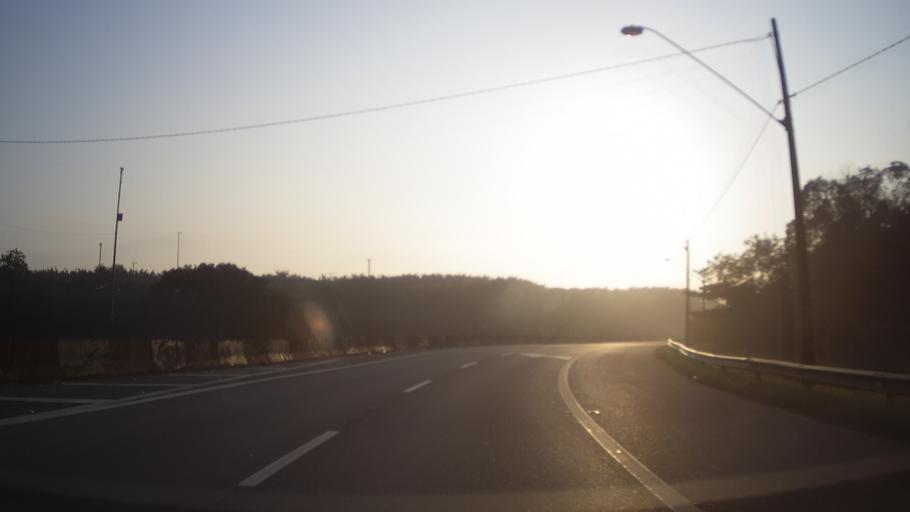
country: BR
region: Sao Paulo
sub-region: Cubatao
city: Cubatao
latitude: -23.9194
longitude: -46.4162
